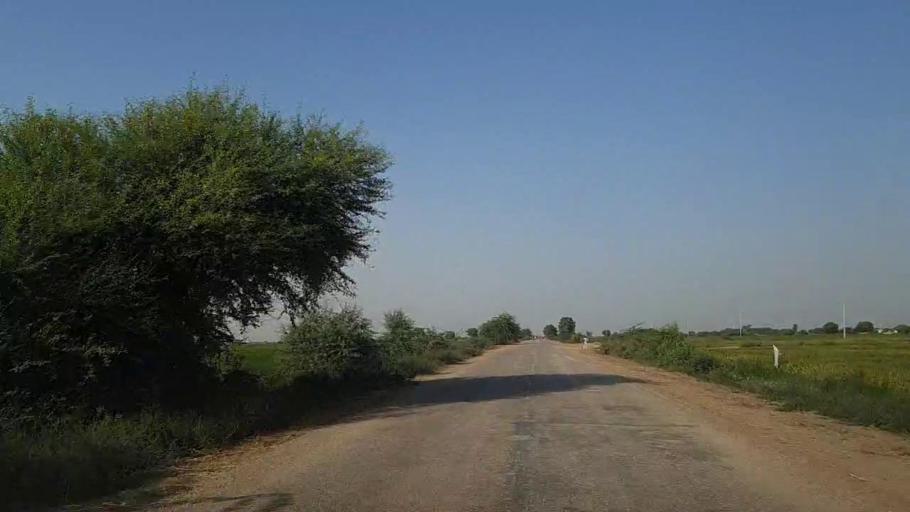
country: PK
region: Sindh
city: Mirpur Batoro
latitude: 24.5839
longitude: 68.3966
